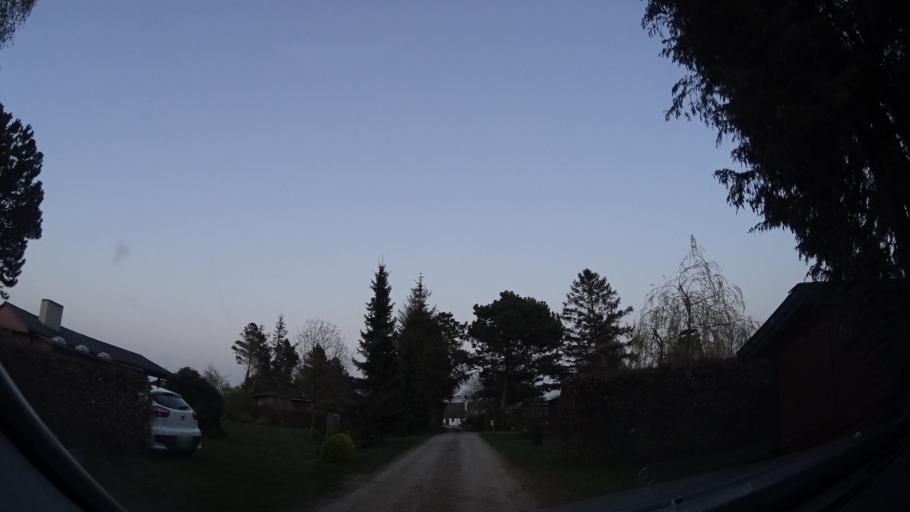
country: DK
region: Zealand
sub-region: Lejre Kommune
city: Ejby
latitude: 55.7098
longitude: 11.8487
